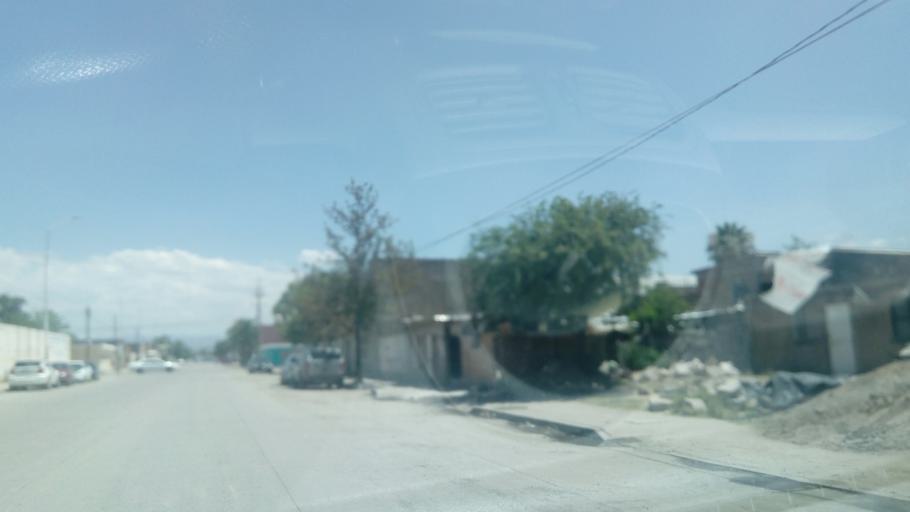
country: MX
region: Durango
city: Victoria de Durango
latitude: 24.0144
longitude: -104.6288
